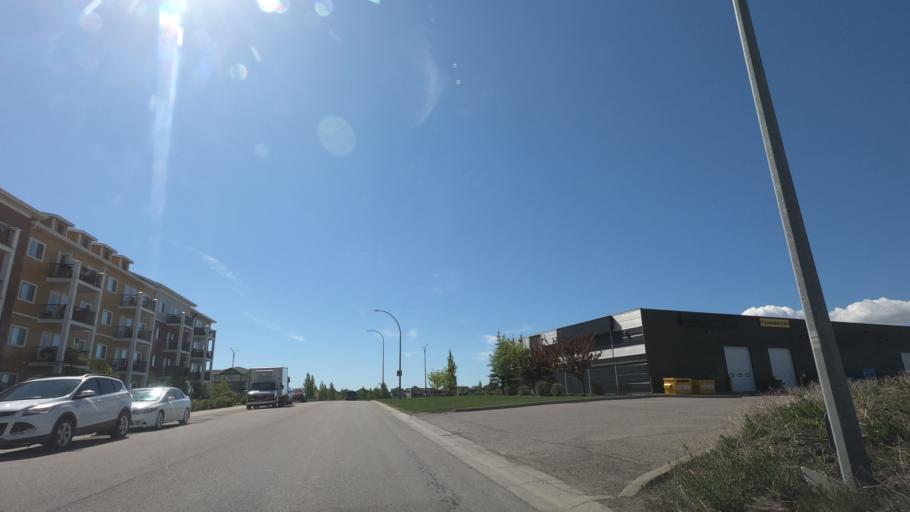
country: CA
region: Alberta
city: Airdrie
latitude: 51.2668
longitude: -113.9944
